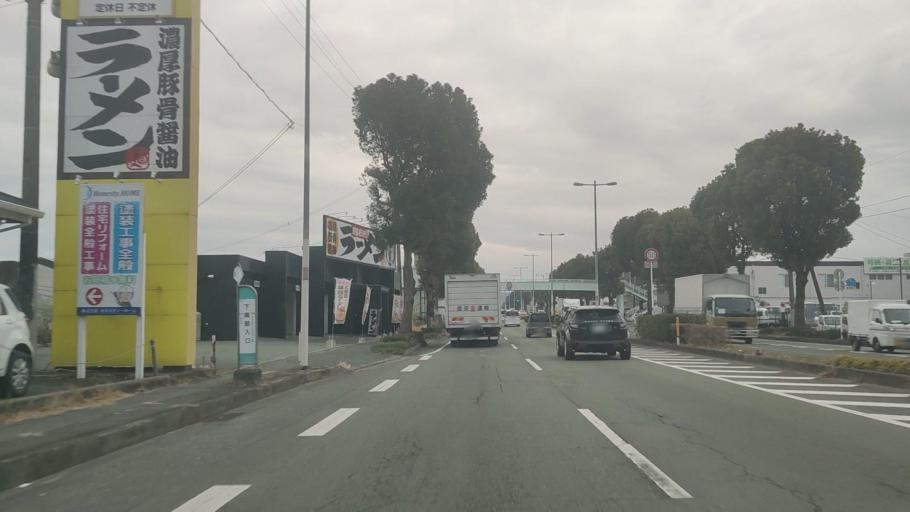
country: JP
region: Kumamoto
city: Kumamoto
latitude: 32.8228
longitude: 130.7609
